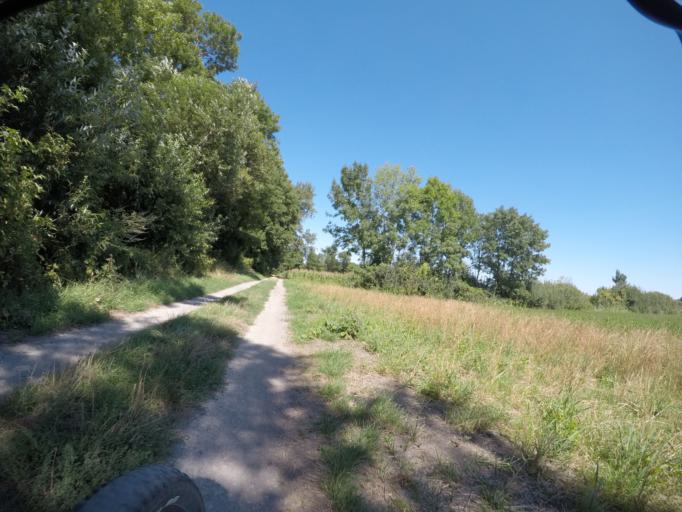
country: AT
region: Lower Austria
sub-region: Politischer Bezirk Wien-Umgebung
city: Moosbrunn
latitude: 48.0071
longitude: 16.4428
